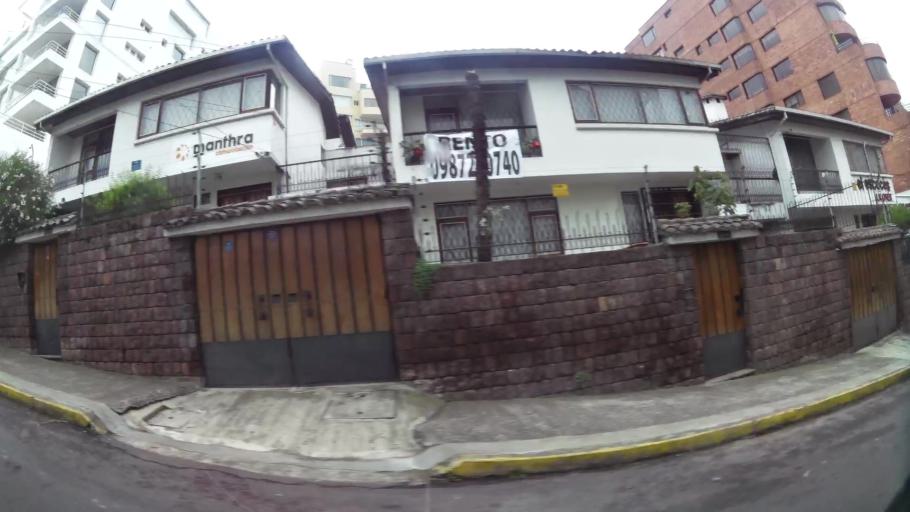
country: EC
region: Pichincha
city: Quito
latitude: -0.1959
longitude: -78.4806
